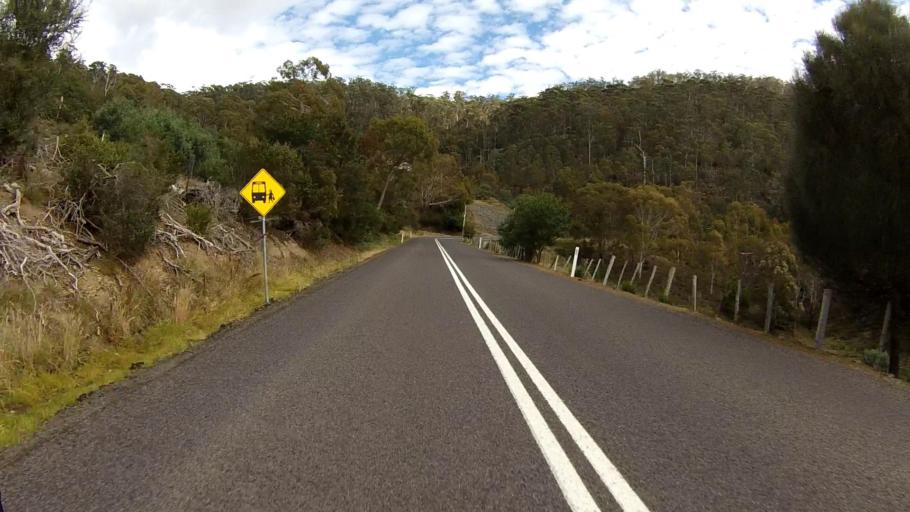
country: AU
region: Tasmania
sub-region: Clarence
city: Lindisfarne
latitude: -42.7847
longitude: 147.3587
